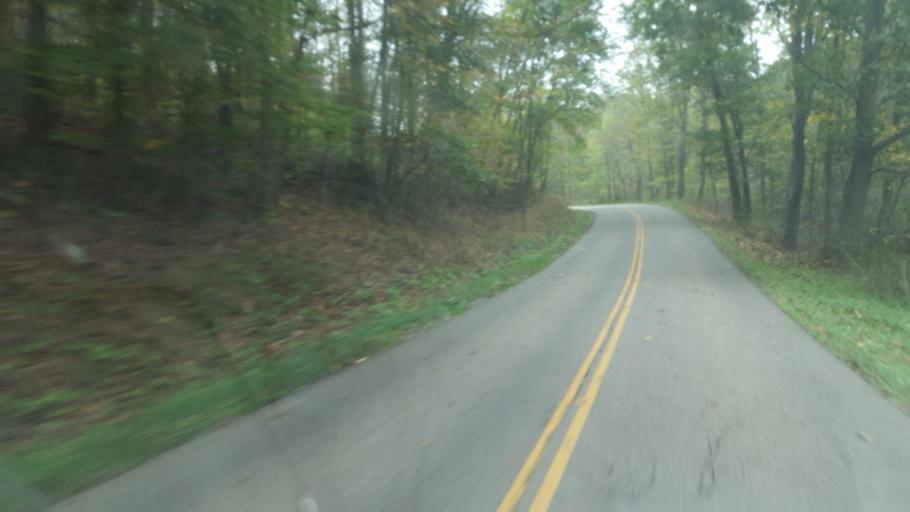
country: US
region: Ohio
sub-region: Carroll County
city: Carrollton
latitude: 40.5296
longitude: -81.1373
